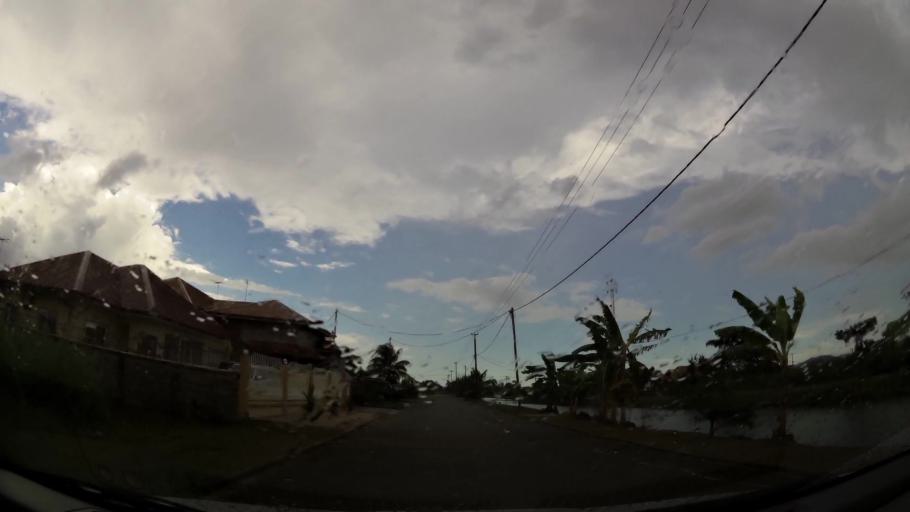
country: SR
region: Commewijne
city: Nieuw Amsterdam
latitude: 5.8560
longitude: -55.1165
